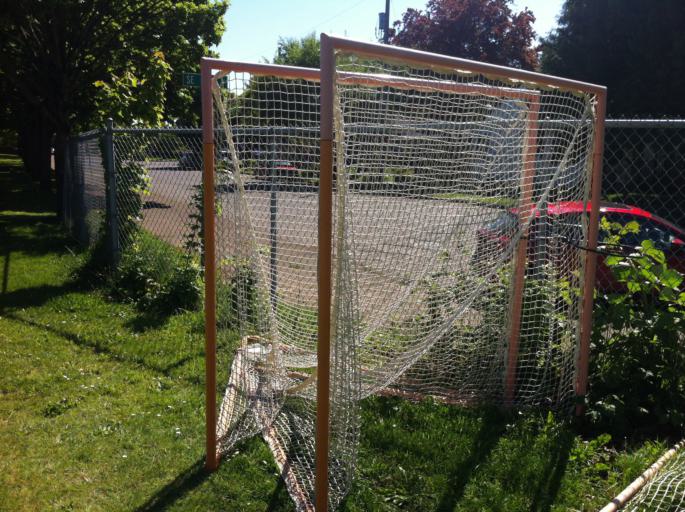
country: US
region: Oregon
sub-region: Multnomah County
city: Lents
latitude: 45.4996
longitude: -122.5922
